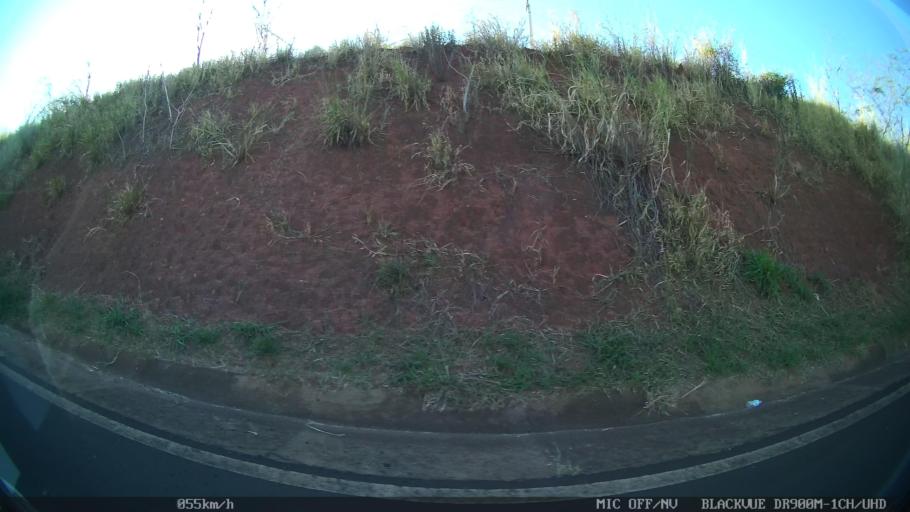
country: BR
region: Sao Paulo
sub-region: Guapiacu
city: Guapiacu
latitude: -20.7823
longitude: -49.2638
